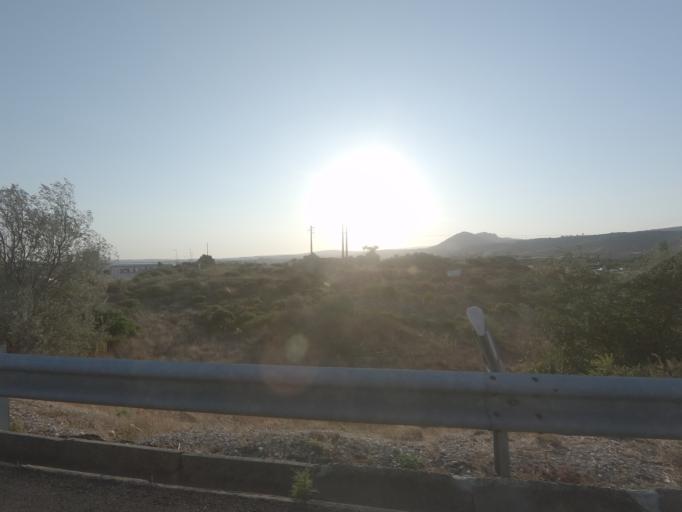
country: PT
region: Santarem
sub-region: Alcanena
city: Alcanena
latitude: 39.4805
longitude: -8.6231
